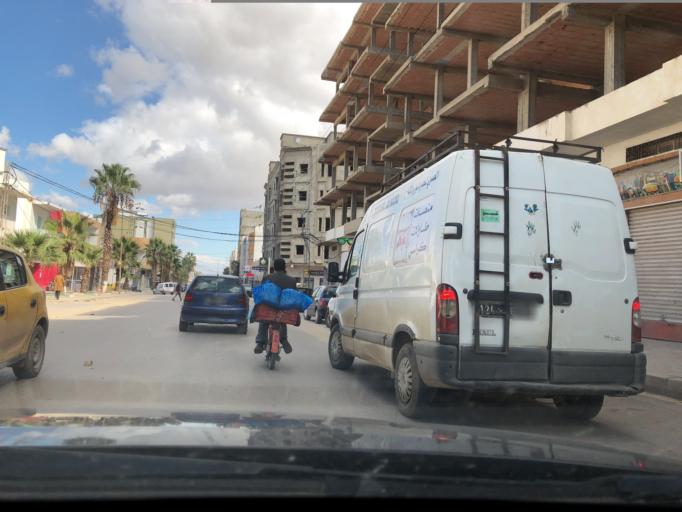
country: TN
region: Al Qasrayn
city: Kasserine
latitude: 35.1699
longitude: 8.8384
